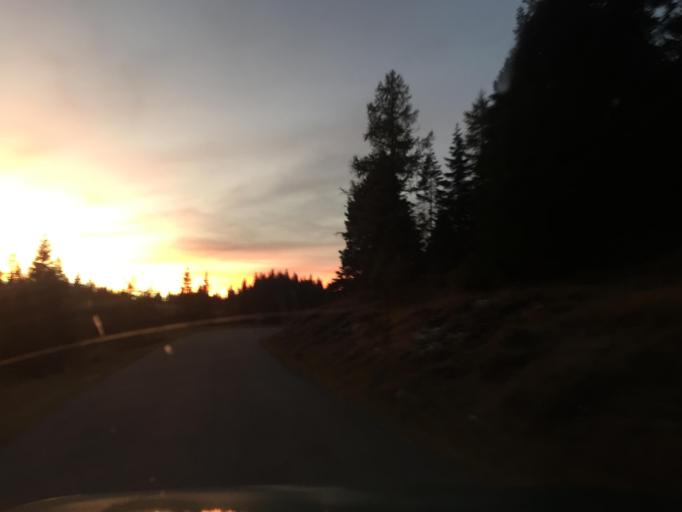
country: IT
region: Veneto
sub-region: Provincia di Belluno
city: Granvilla
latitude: 46.6225
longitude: 12.7121
